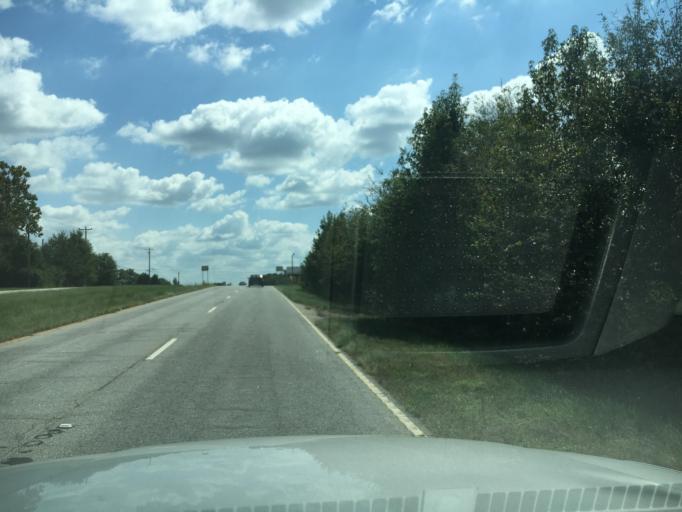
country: US
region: South Carolina
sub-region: Greenwood County
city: Greenwood
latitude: 34.2651
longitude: -82.2274
